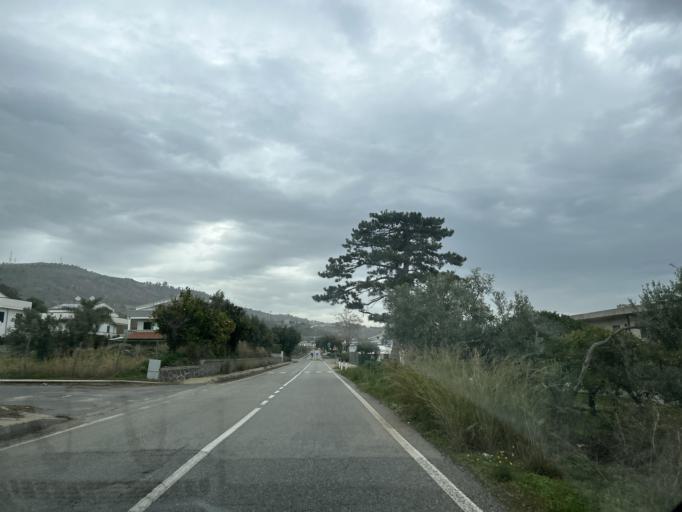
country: IT
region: Calabria
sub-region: Provincia di Catanzaro
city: Montepaone Lido
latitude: 38.7353
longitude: 16.5455
